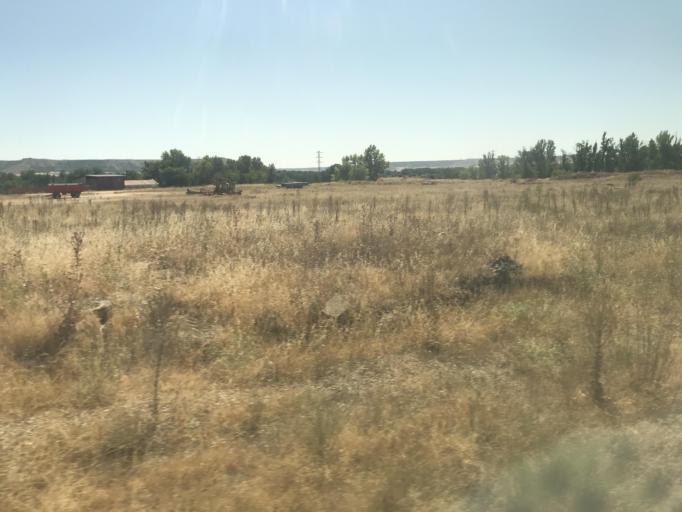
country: ES
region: Castille and Leon
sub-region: Provincia de Palencia
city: Duenas
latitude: 41.8347
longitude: -4.5634
